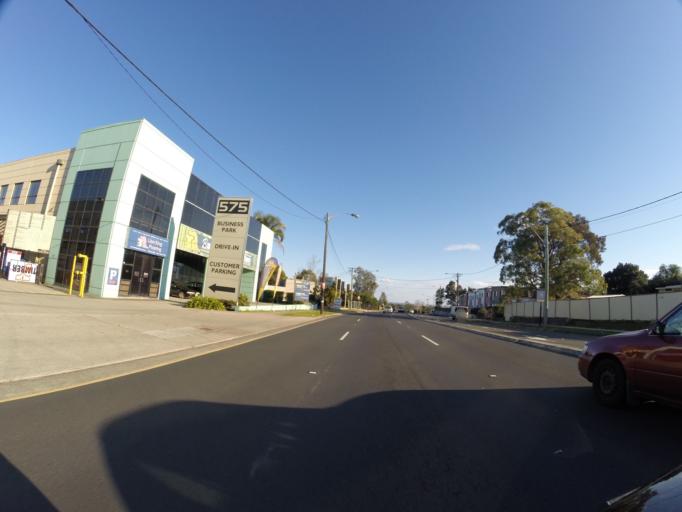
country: AU
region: New South Wales
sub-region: Holroyd
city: Guildford West
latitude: -33.8629
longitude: 150.9916
